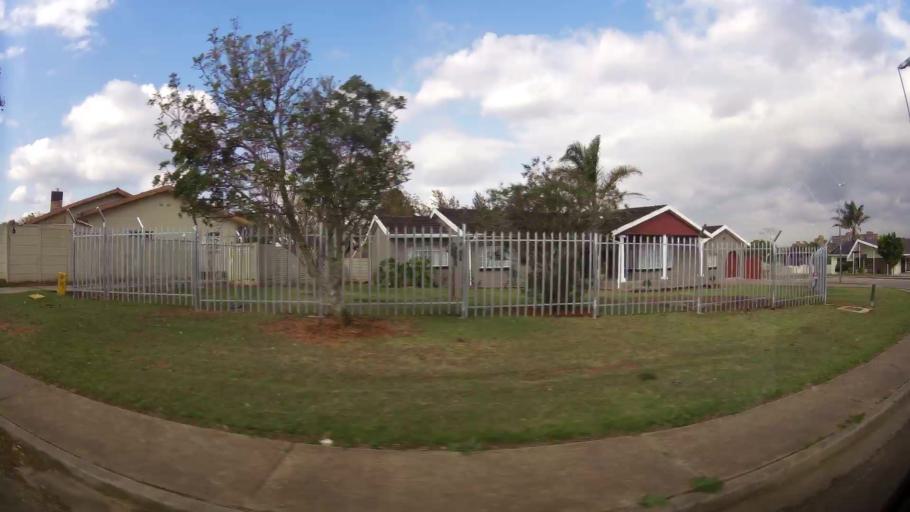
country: ZA
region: Eastern Cape
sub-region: Nelson Mandela Bay Metropolitan Municipality
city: Uitenhage
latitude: -33.7342
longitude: 25.4061
